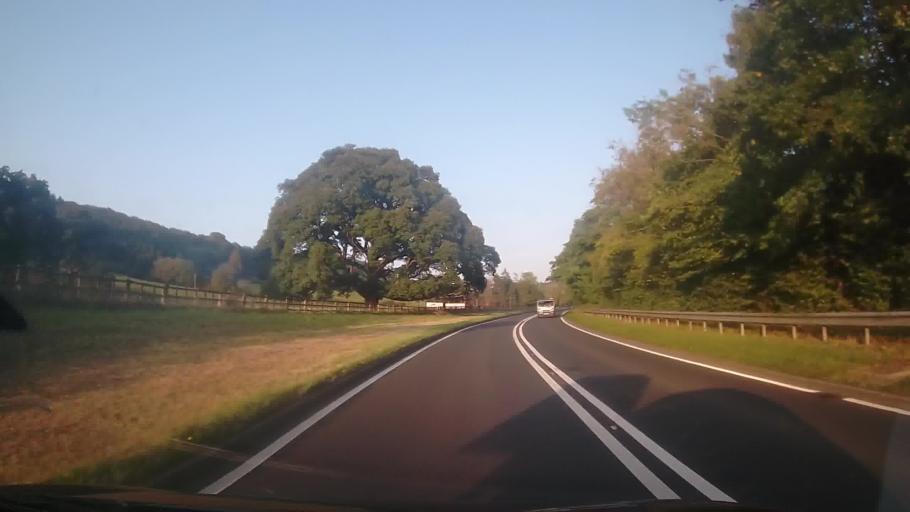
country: GB
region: Wales
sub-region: Sir Powys
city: Montgomery
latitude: 52.5639
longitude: -3.2264
